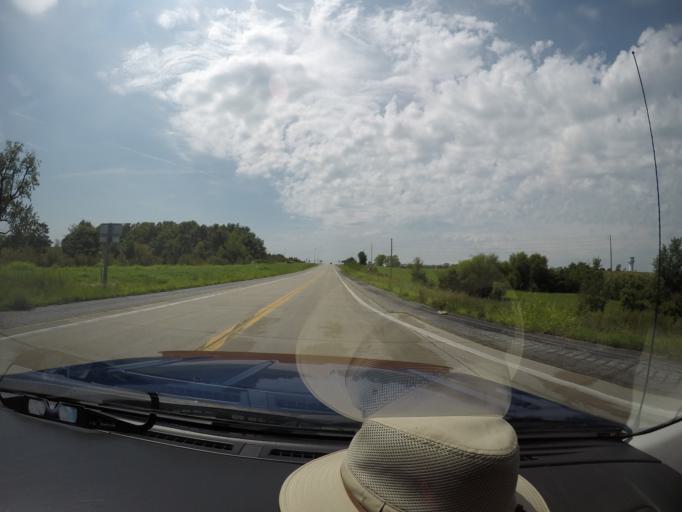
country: US
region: Missouri
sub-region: Lafayette County
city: Lexington
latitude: 39.1849
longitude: -93.8429
